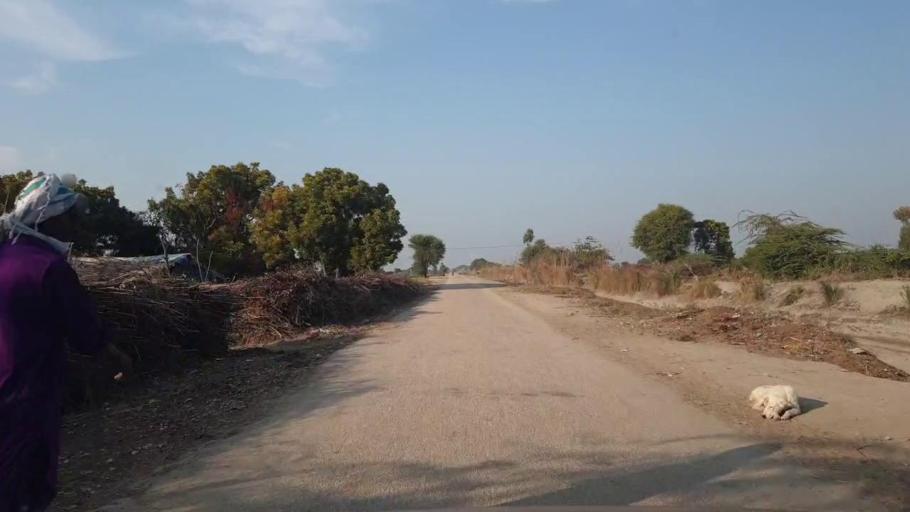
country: PK
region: Sindh
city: Shahpur Chakar
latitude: 26.1584
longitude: 68.6406
